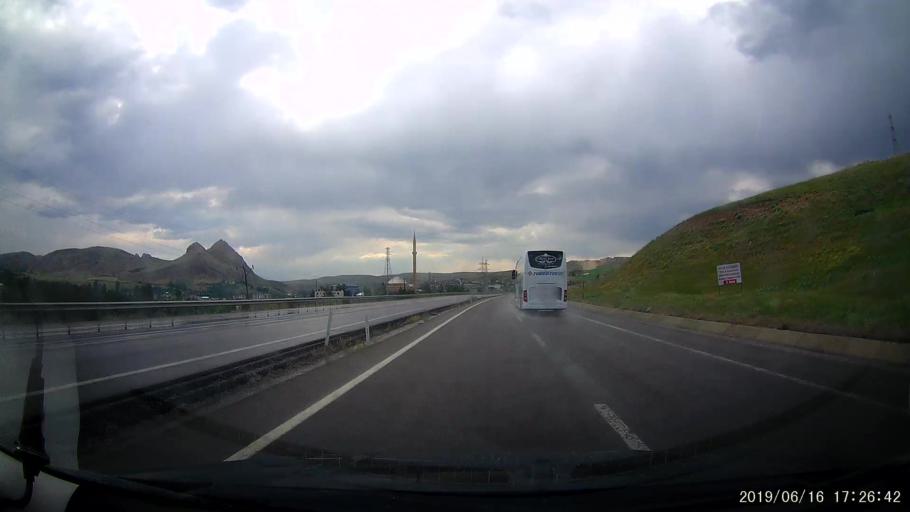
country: TR
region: Erzincan
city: Tercan
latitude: 39.7707
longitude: 40.4067
